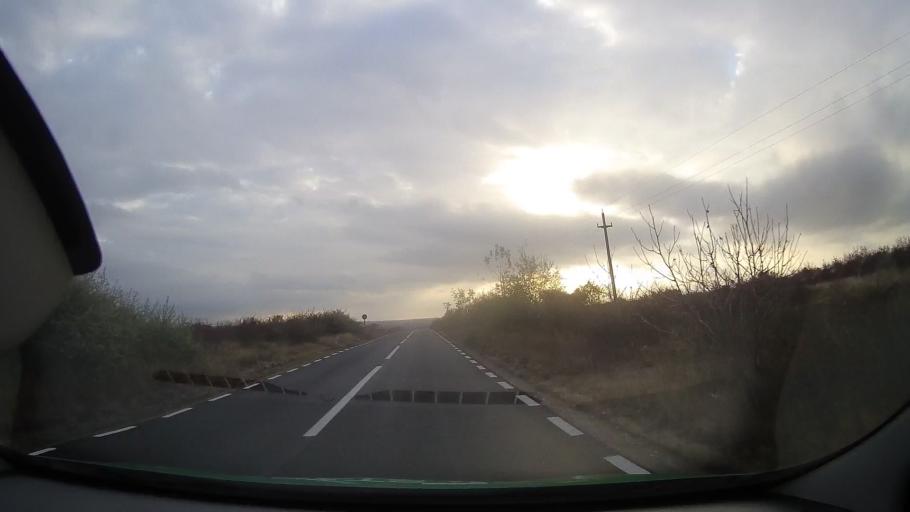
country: RO
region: Constanta
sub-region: Comuna Adamclisi
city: Adamclisi
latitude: 44.0662
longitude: 27.9745
